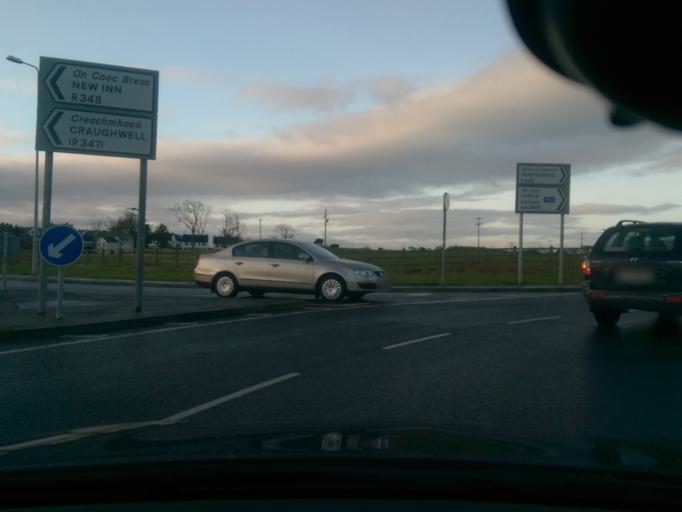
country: IE
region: Connaught
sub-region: County Galway
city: Athenry
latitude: 53.2937
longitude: -8.7431
